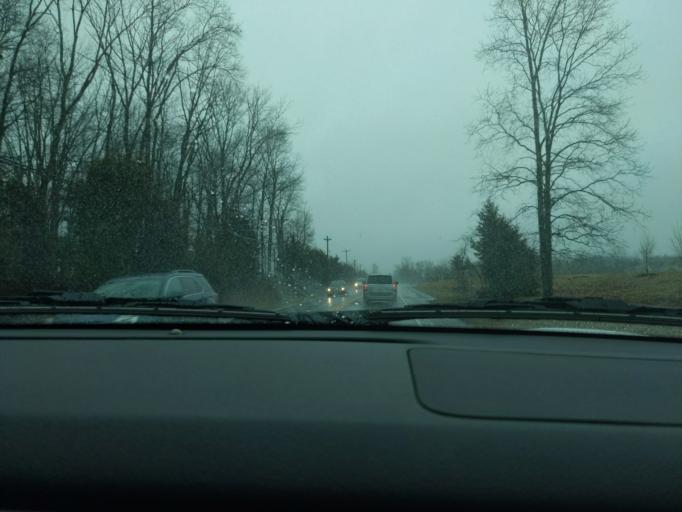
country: US
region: Pennsylvania
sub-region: Bucks County
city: Dublin
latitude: 40.3871
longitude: -75.2273
